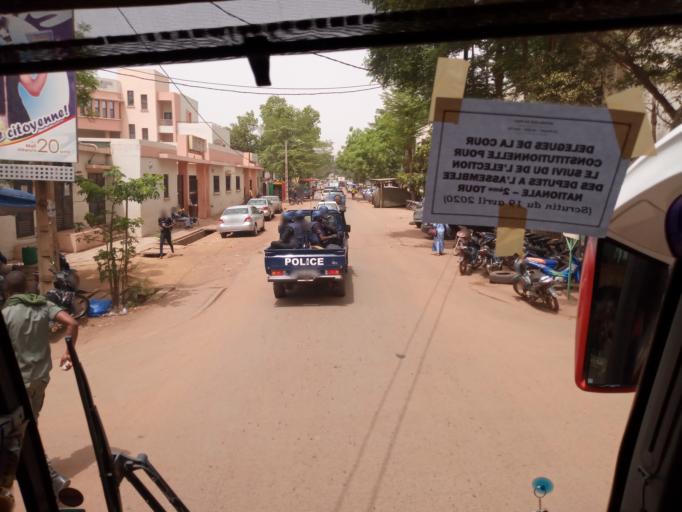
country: ML
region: Bamako
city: Bamako
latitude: 12.6382
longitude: -7.9989
